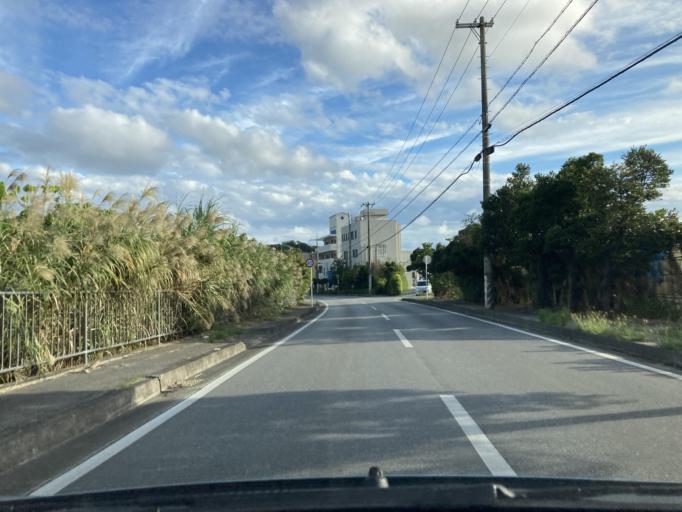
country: JP
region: Okinawa
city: Tomigusuku
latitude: 26.1544
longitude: 127.7413
